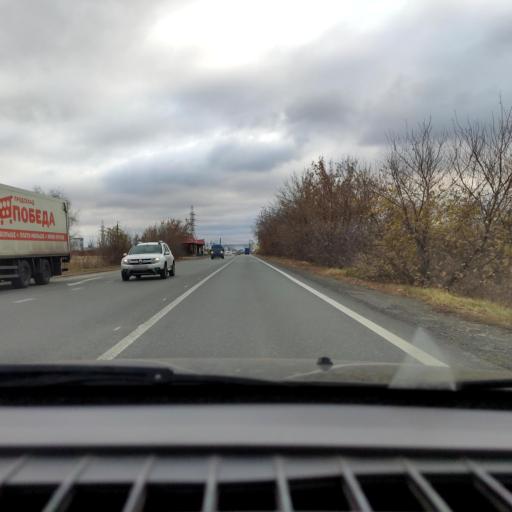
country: RU
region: Samara
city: Tol'yatti
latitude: 53.5473
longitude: 49.3773
